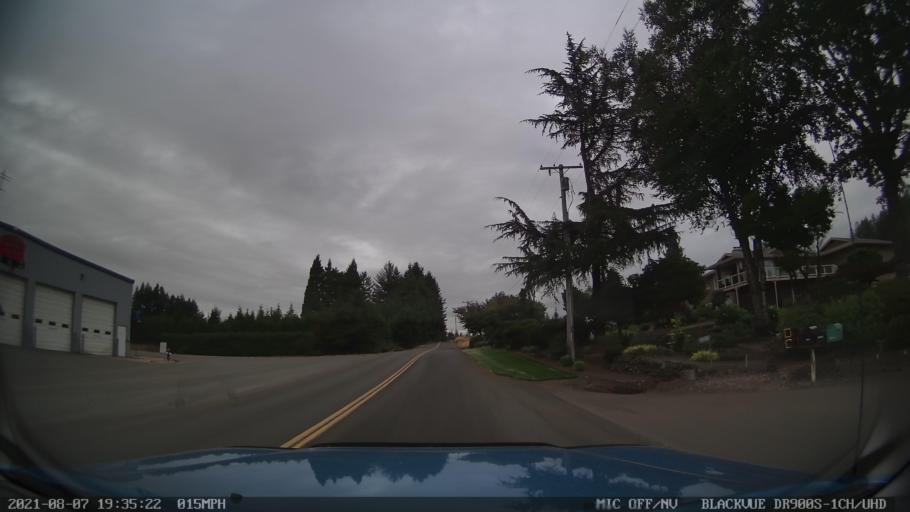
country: US
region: Oregon
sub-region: Marion County
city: Silverton
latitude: 44.9262
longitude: -122.6567
